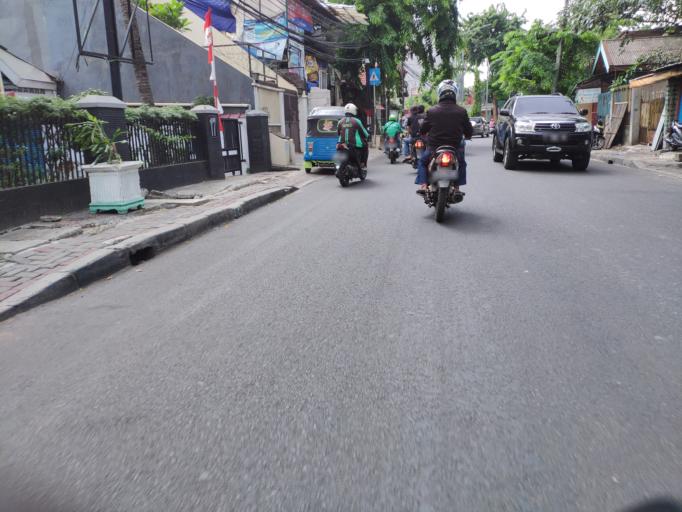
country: ID
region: Jakarta Raya
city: Jakarta
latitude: -6.1938
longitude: 106.8634
